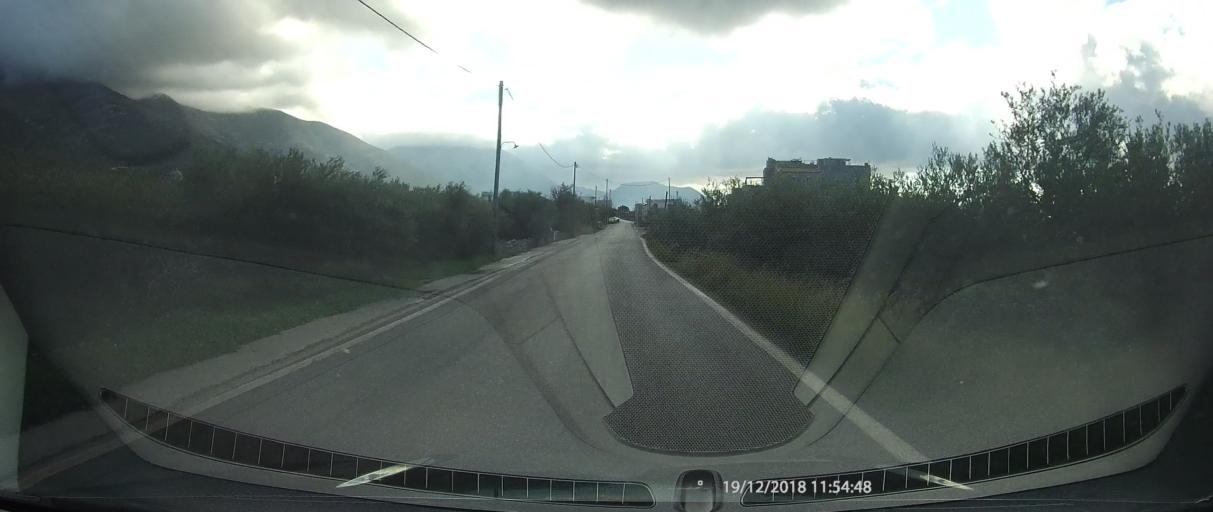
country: GR
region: Peloponnese
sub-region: Nomos Lakonias
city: Gytheio
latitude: 36.6139
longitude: 22.3910
